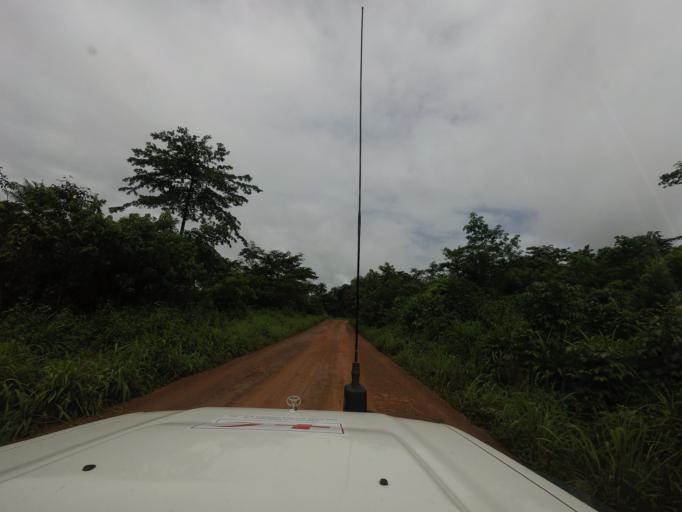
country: GN
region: Nzerekore
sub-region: Nzerekore Prefecture
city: Nzerekore
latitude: 7.7266
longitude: -8.8692
